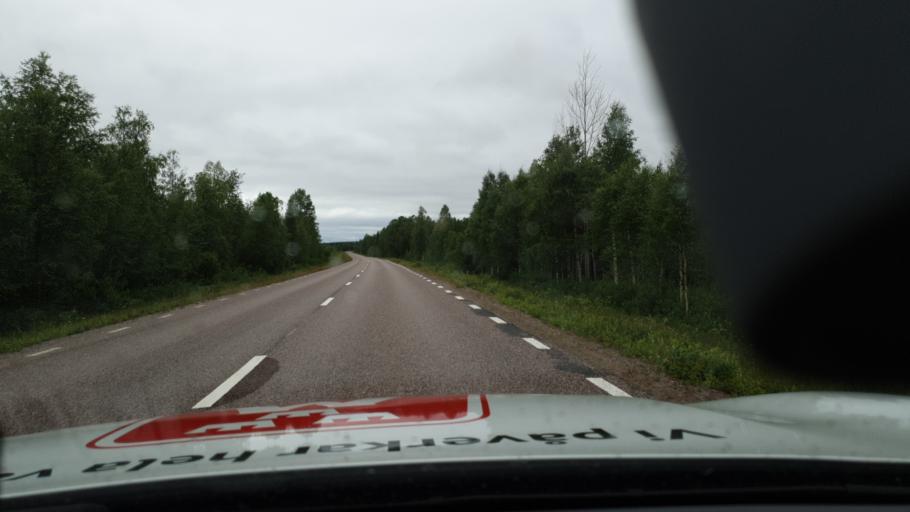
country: SE
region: Norrbotten
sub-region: Pajala Kommun
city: Pajala
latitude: 67.1983
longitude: 23.4369
